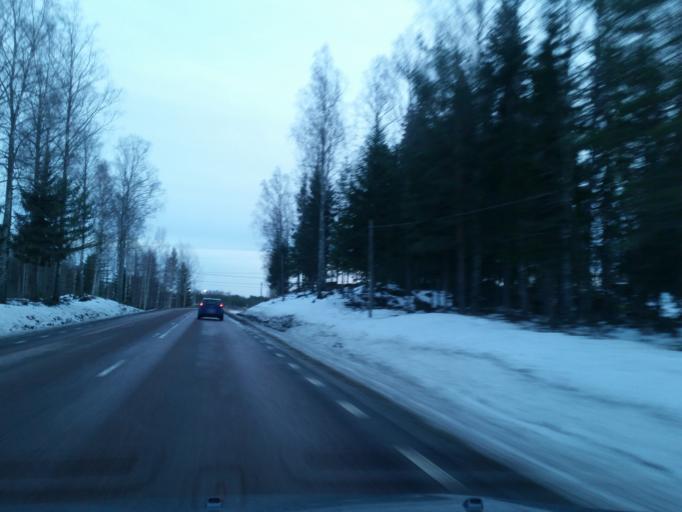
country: SE
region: Gaevleborg
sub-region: Sandvikens Kommun
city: Sandviken
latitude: 60.6350
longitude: 16.7448
